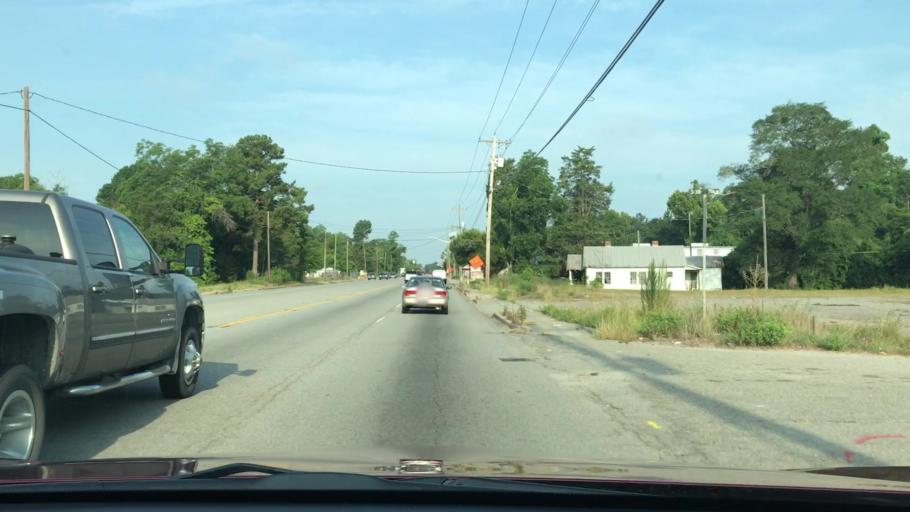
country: US
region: South Carolina
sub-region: Orangeburg County
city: Edisto
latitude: 33.4812
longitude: -80.8927
